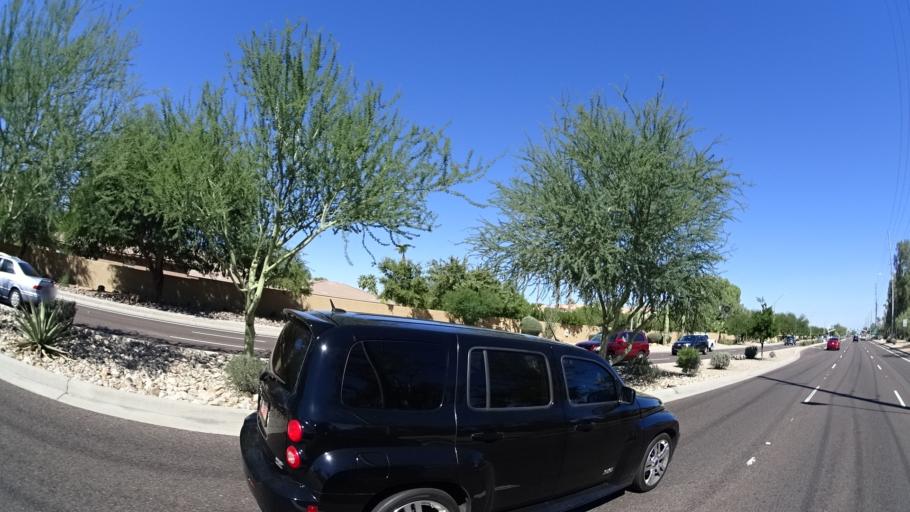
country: US
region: Arizona
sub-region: Maricopa County
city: Paradise Valley
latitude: 33.5718
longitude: -111.9260
